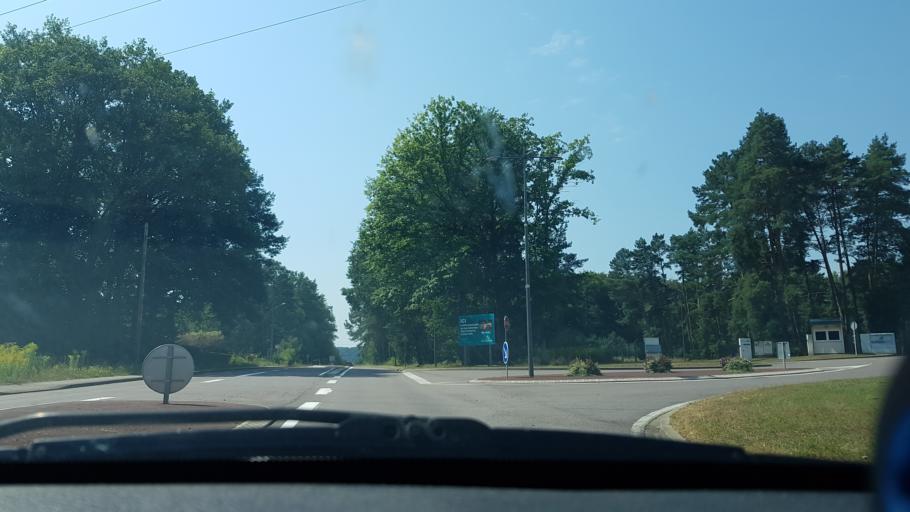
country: FR
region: Lorraine
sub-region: Departement de la Moselle
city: Porcelette
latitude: 49.1684
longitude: 6.6624
